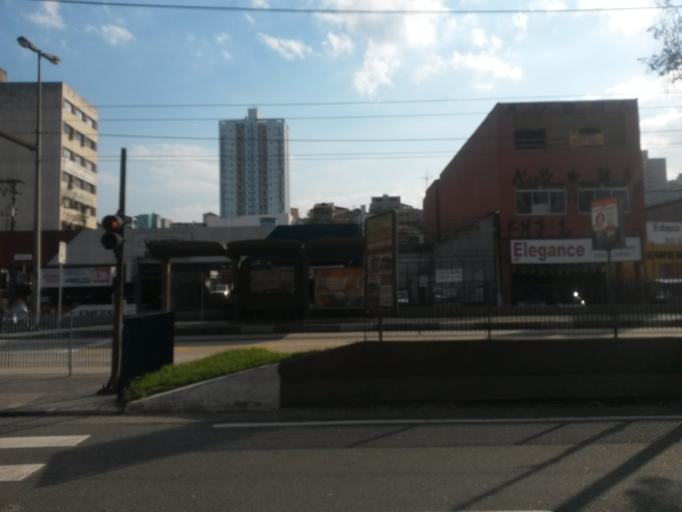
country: BR
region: Sao Paulo
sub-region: Sao Bernardo Do Campo
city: Sao Bernardo do Campo
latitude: -23.7118
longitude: -46.5521
